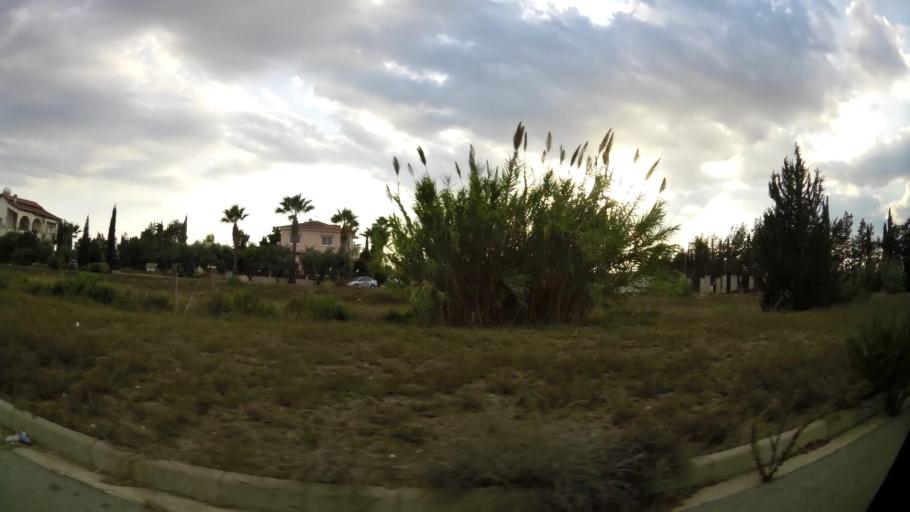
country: CY
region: Larnaka
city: Meneou
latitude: 34.8581
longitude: 33.5884
